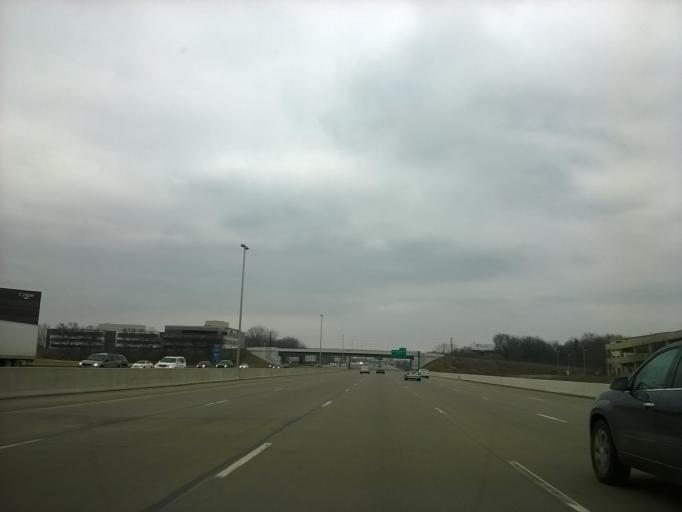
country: US
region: Indiana
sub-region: Hamilton County
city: Carmel
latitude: 39.9180
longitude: -86.1012
